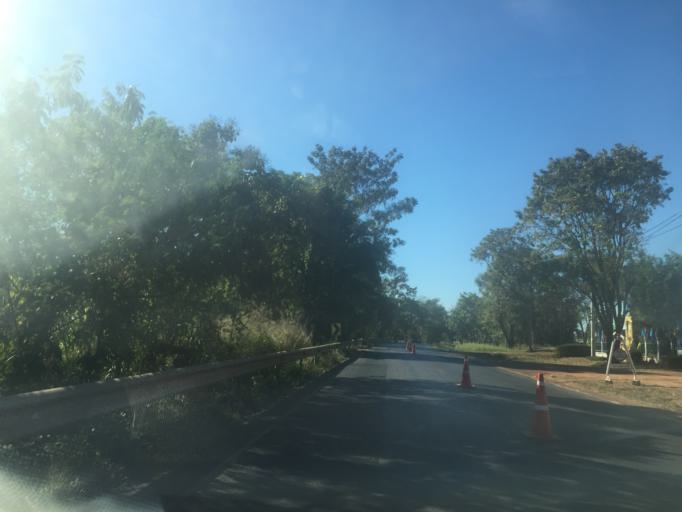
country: TH
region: Kalasin
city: Tha Khantho
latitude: 16.9637
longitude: 103.2493
